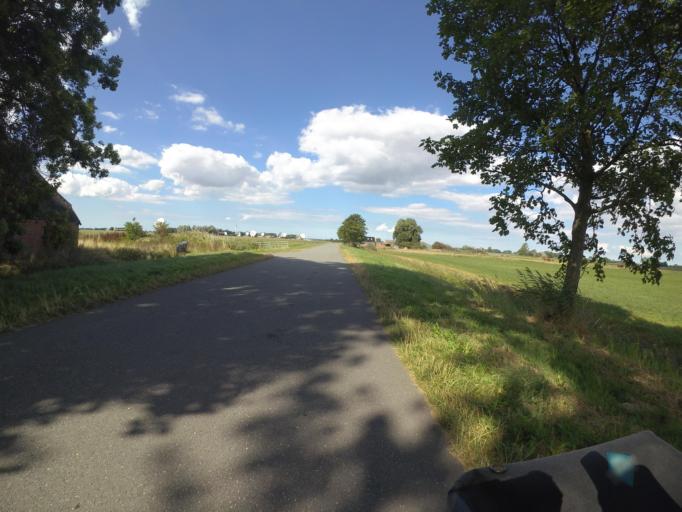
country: NL
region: Friesland
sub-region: Gemeente Kollumerland en Nieuwkruisland
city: Kollum
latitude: 53.2772
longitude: 6.2233
